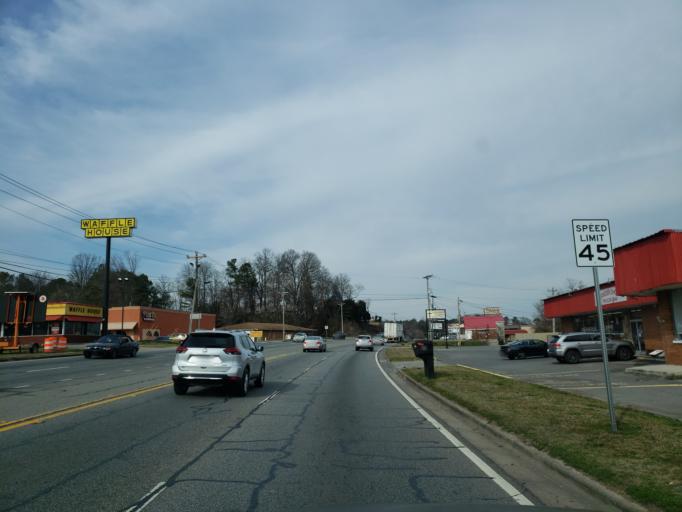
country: US
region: Georgia
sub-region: Whitfield County
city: Dalton
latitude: 34.8007
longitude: -84.9617
